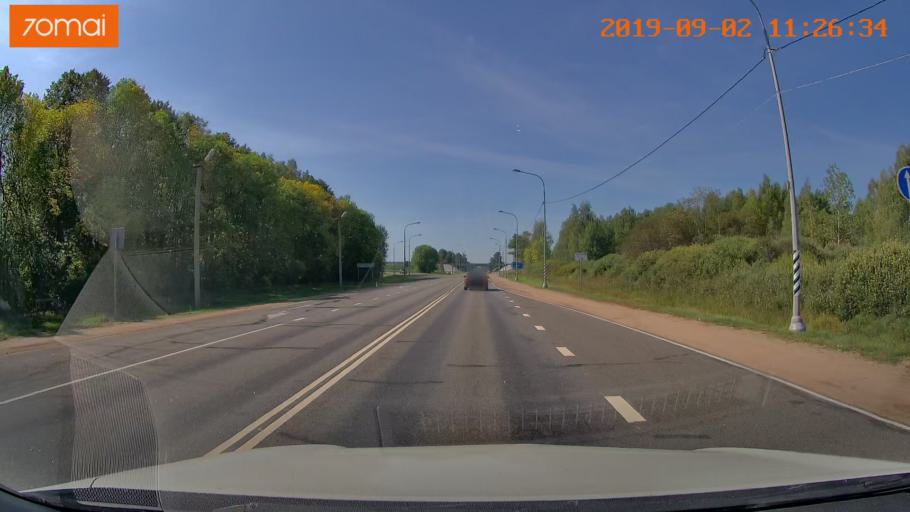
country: RU
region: Smolensk
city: Roslavl'
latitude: 53.9917
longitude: 32.9294
